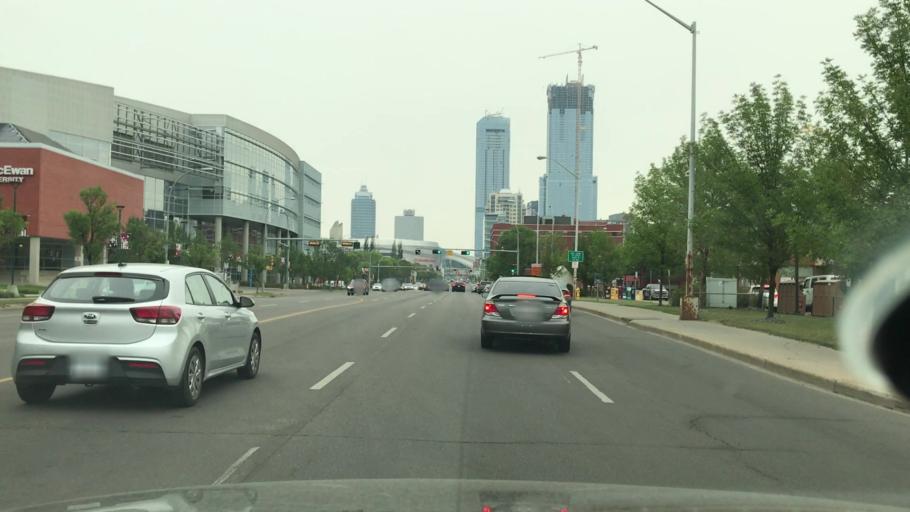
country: CA
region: Alberta
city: Edmonton
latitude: 53.5462
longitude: -113.5120
